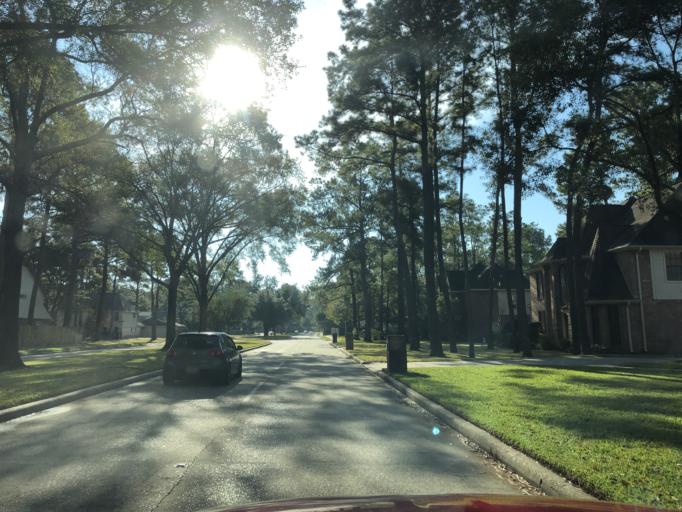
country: US
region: Texas
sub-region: Harris County
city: Tomball
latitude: 30.0208
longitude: -95.5467
